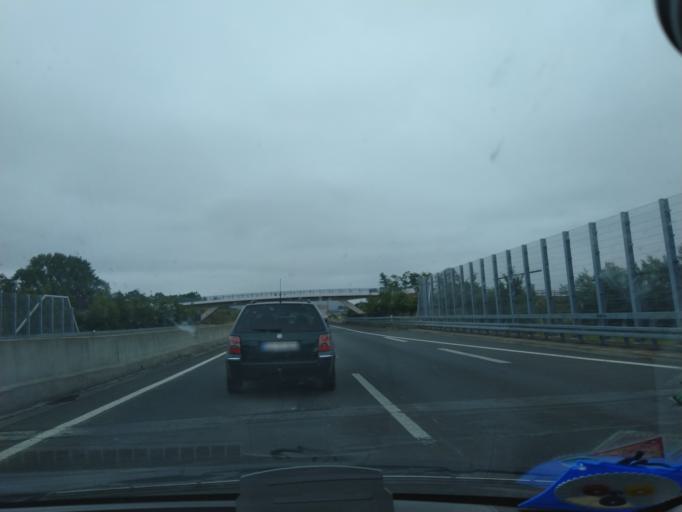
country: DE
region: North Rhine-Westphalia
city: Bad Oeynhausen
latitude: 52.2330
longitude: 8.7963
